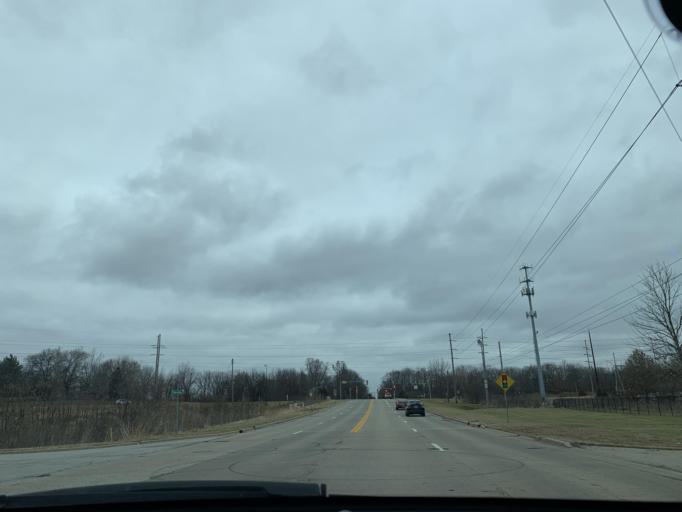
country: US
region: Illinois
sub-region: Sangamon County
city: Leland Grove
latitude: 39.8230
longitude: -89.6872
